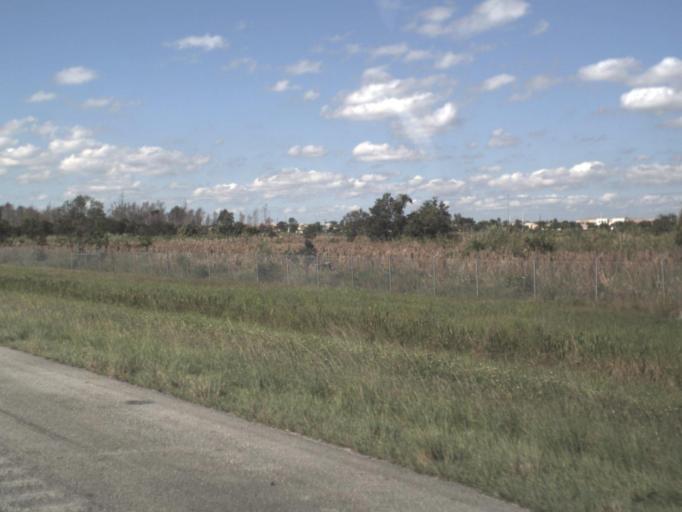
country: US
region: Florida
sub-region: Miami-Dade County
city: Country Club
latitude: 25.9611
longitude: -80.3366
